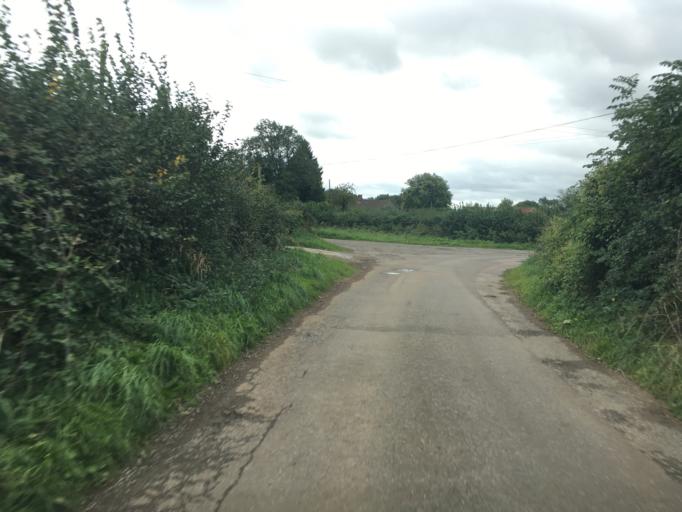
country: GB
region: England
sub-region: South Gloucestershire
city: Tytherington
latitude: 51.5970
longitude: -2.4753
